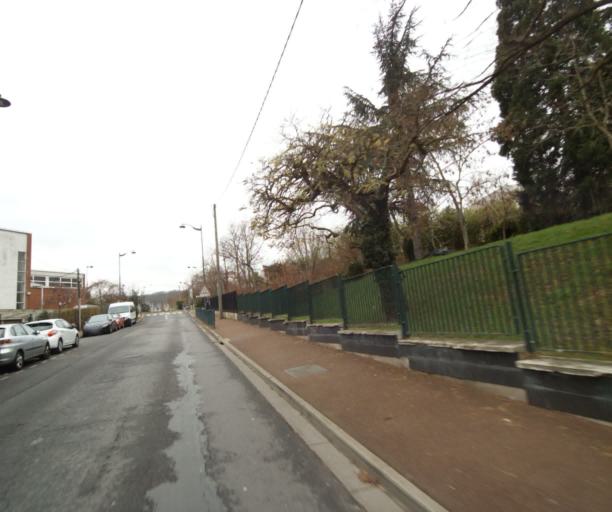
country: FR
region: Ile-de-France
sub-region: Departement des Hauts-de-Seine
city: Rueil-Malmaison
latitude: 48.8656
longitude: 2.1798
